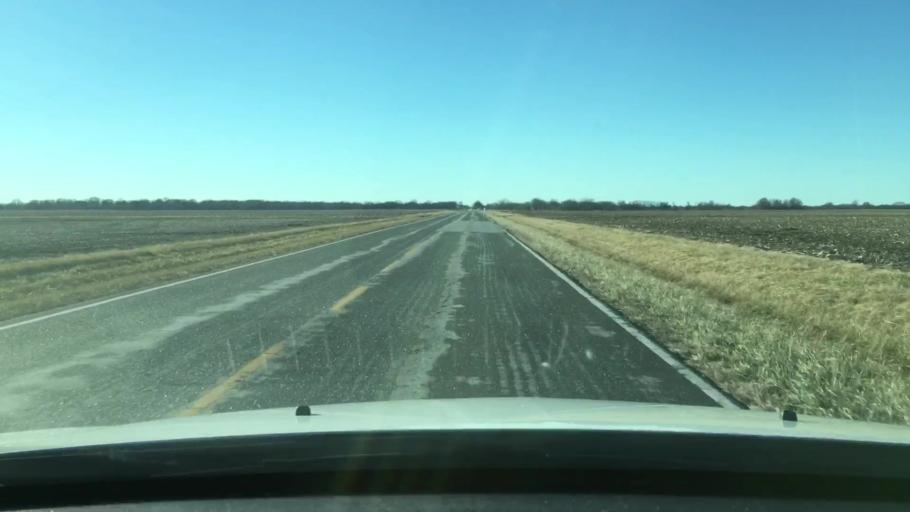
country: US
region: Missouri
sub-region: Audrain County
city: Vandalia
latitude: 39.2815
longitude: -91.6949
